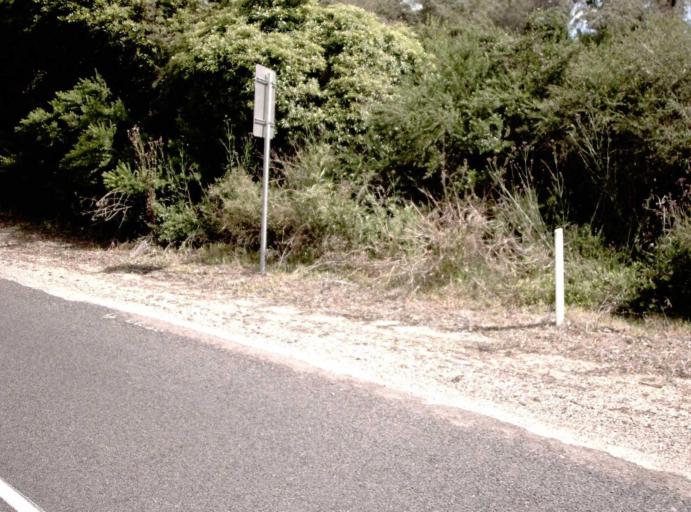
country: AU
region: New South Wales
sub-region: Bega Valley
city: Eden
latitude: -37.4806
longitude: 149.5989
